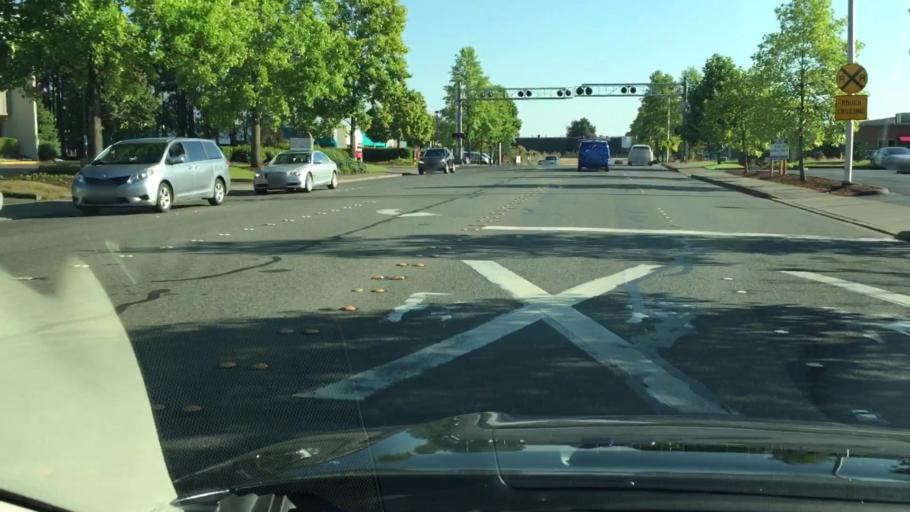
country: US
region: Washington
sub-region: King County
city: Tukwila
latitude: 47.4554
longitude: -122.2500
